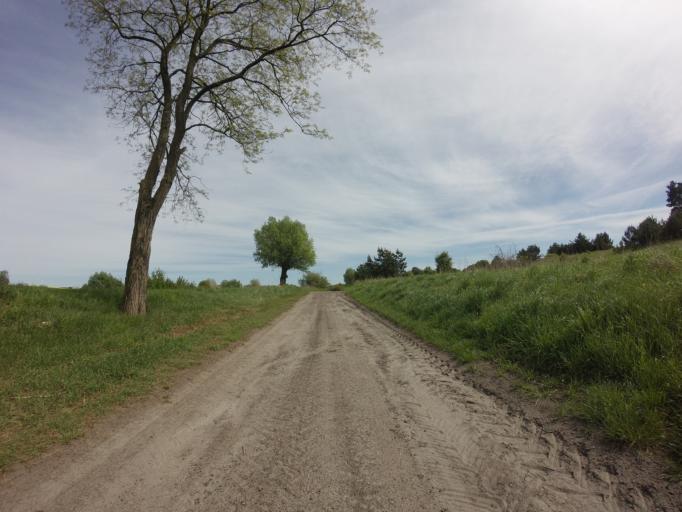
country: PL
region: West Pomeranian Voivodeship
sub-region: Powiat choszczenski
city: Recz
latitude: 53.1756
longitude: 15.5497
